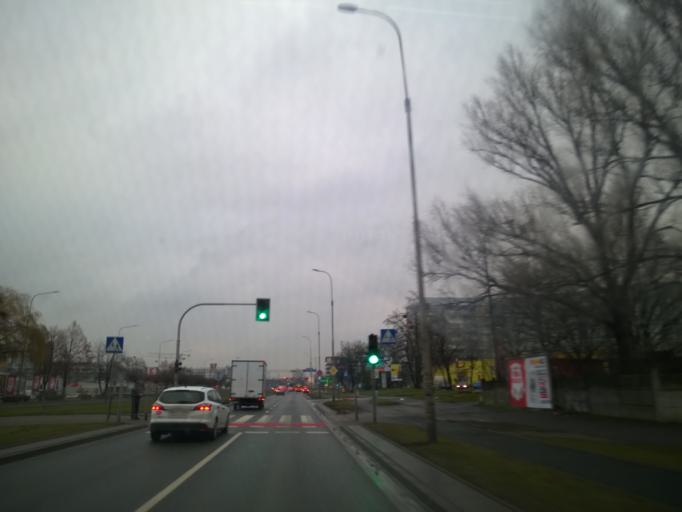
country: PL
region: Lower Silesian Voivodeship
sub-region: Powiat wroclawski
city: Wroclaw
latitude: 51.0830
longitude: 17.0451
